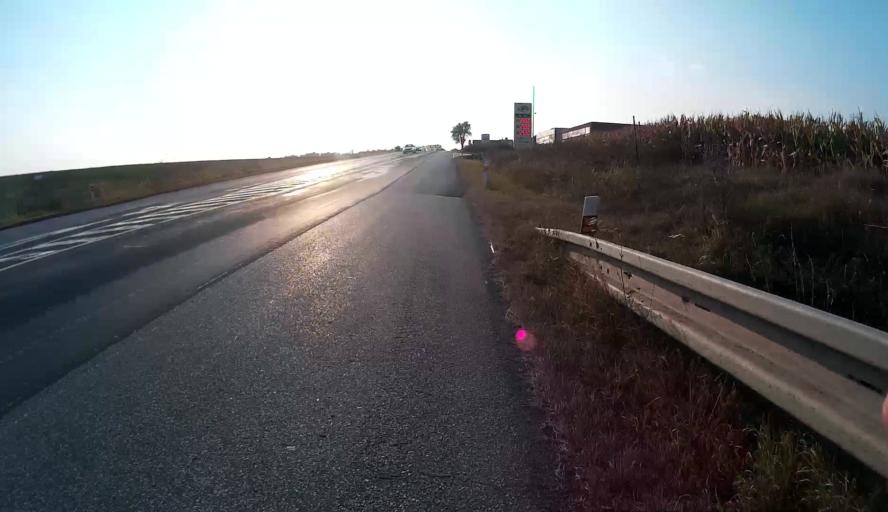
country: CZ
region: South Moravian
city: Podoli
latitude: 49.1825
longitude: 16.7028
